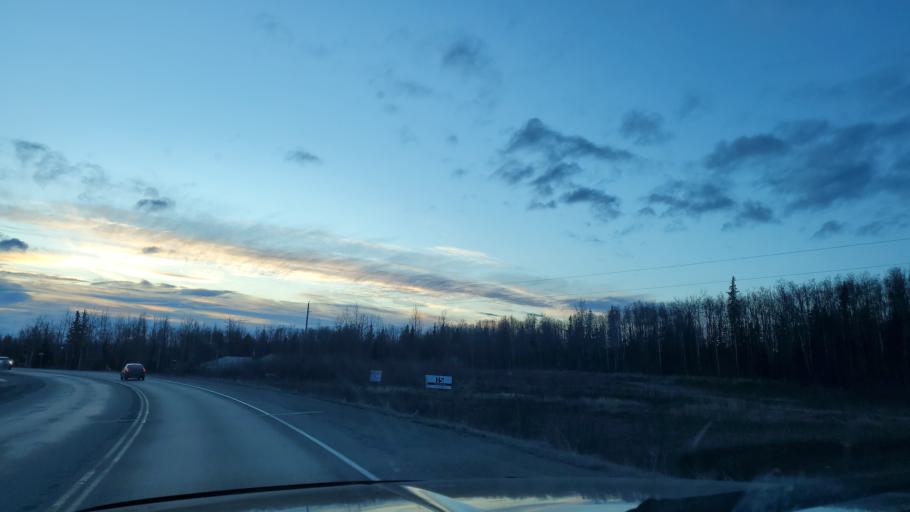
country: US
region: Alaska
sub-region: Matanuska-Susitna Borough
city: Wasilla
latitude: 61.5937
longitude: -149.4374
